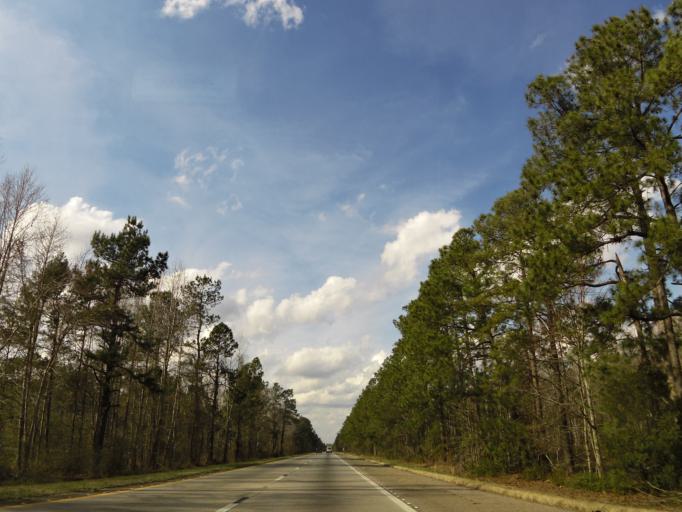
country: US
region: South Carolina
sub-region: Dorchester County
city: Ridgeville
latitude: 33.1938
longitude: -80.3928
